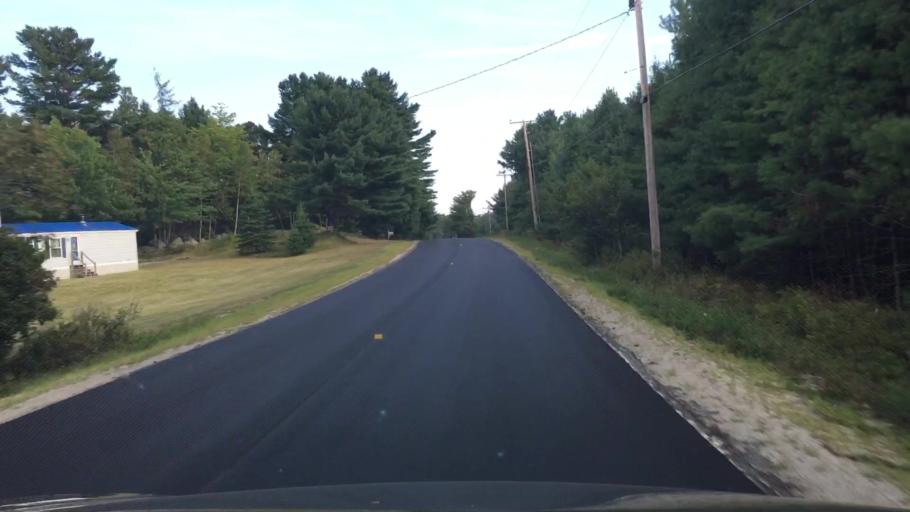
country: US
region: Maine
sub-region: Hancock County
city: Surry
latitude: 44.5295
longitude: -68.6121
